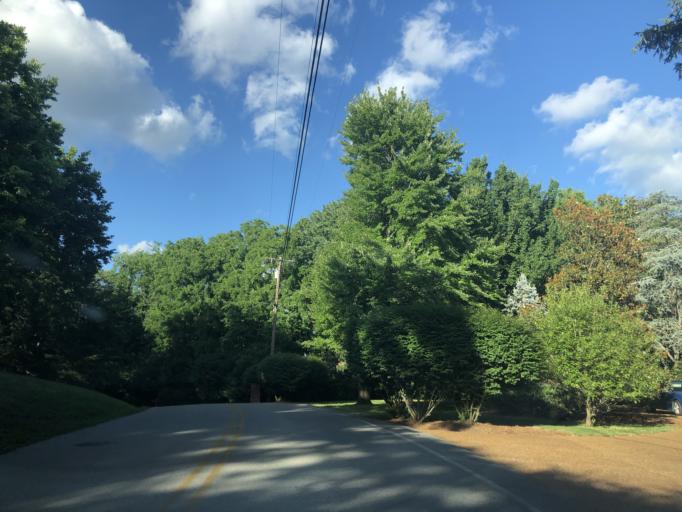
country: US
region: Tennessee
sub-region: Davidson County
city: Forest Hills
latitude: 36.0692
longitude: -86.8189
